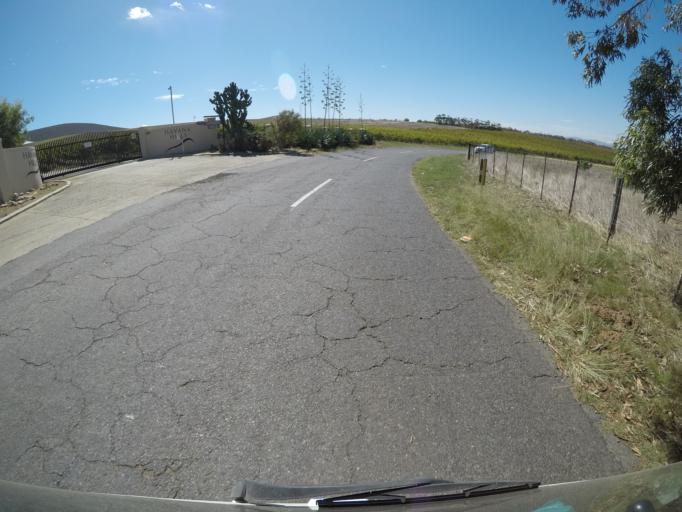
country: ZA
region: Western Cape
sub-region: City of Cape Town
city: Sunset Beach
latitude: -33.7228
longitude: 18.5698
